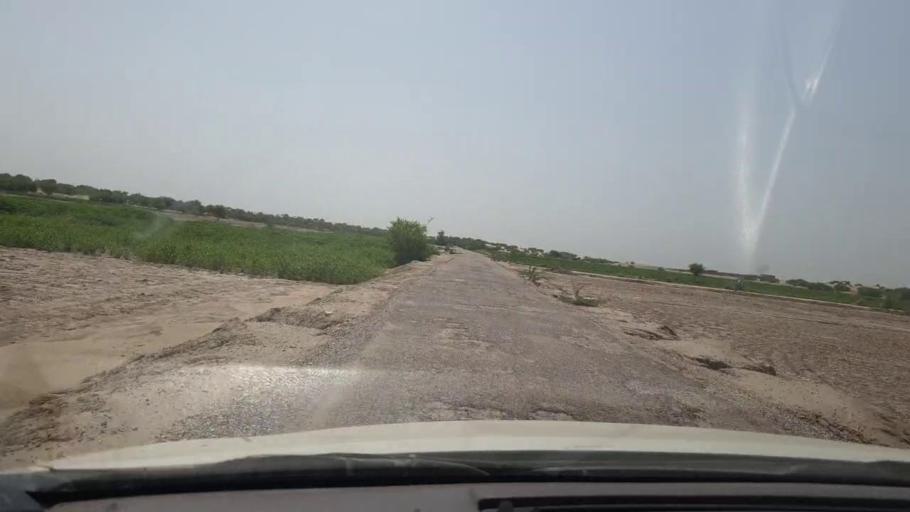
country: PK
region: Sindh
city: Rohri
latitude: 27.5184
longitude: 69.0812
